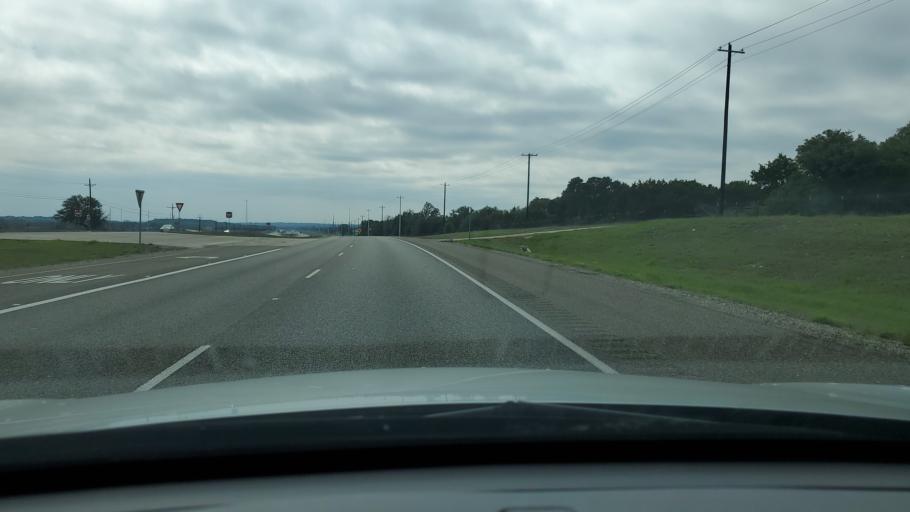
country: US
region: Texas
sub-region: Williamson County
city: Florence
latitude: 30.7943
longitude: -97.7672
